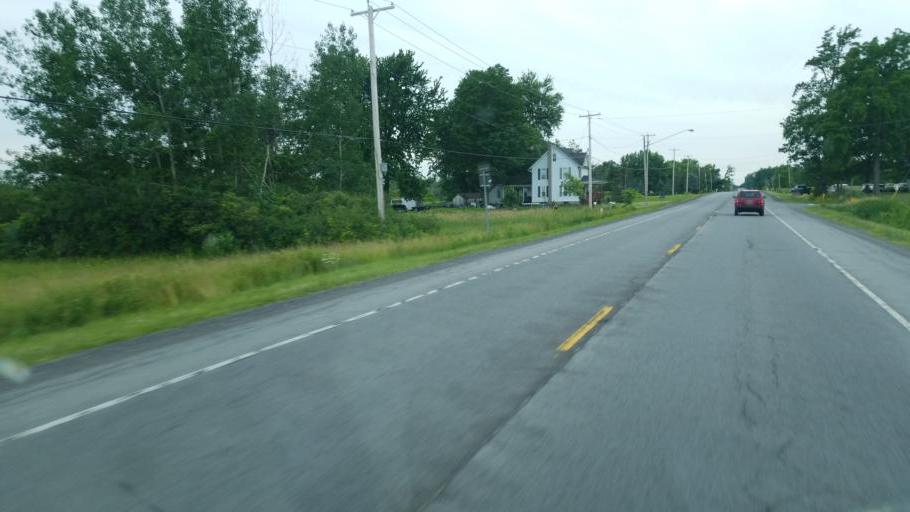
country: US
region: New York
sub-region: Genesee County
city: Oakfield
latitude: 42.9970
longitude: -78.3545
